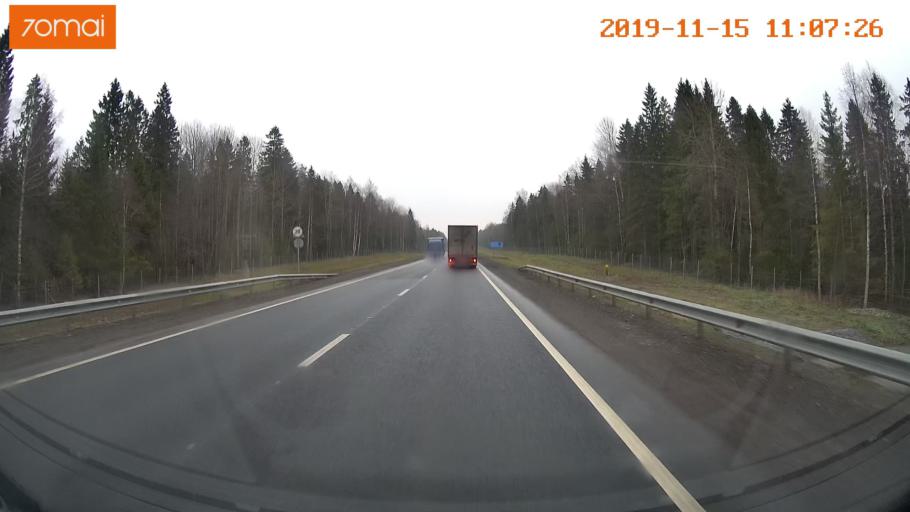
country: RU
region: Vologda
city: Chebsara
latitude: 59.1195
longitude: 39.0506
